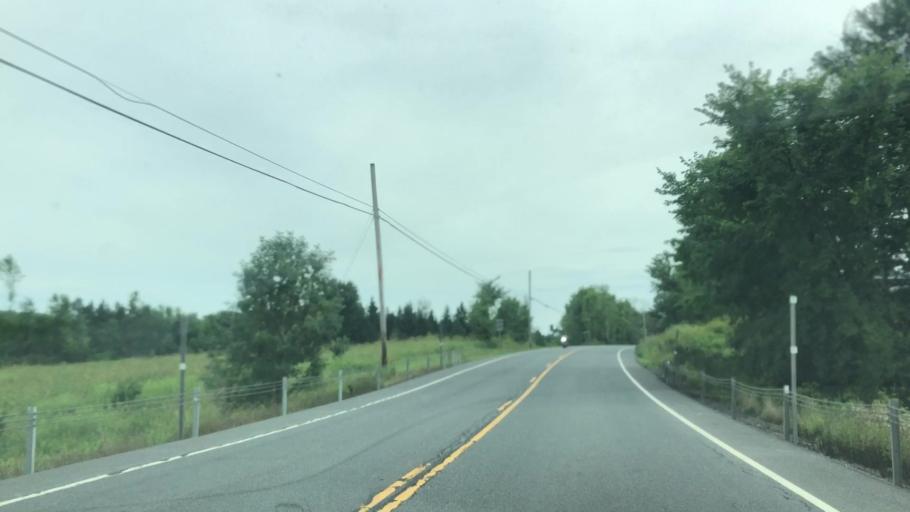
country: US
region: New York
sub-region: Washington County
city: Whitehall
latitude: 43.5112
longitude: -73.4172
